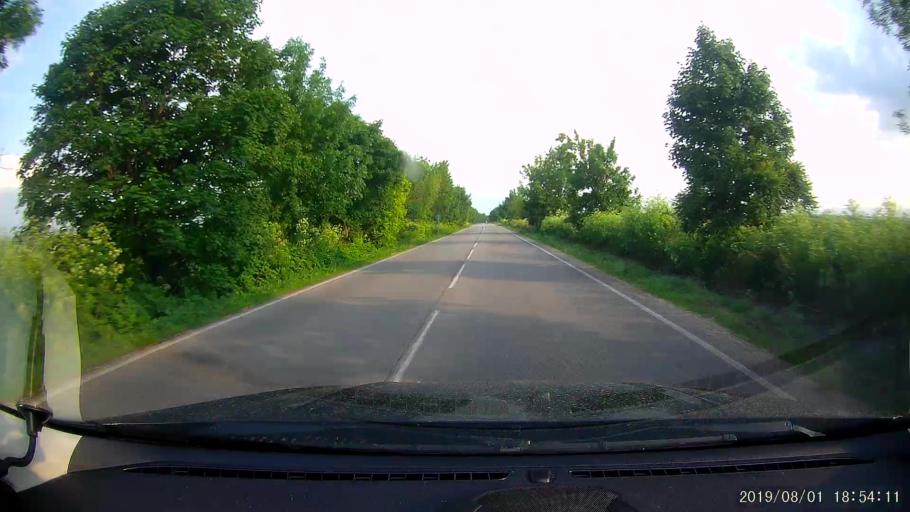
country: BG
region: Shumen
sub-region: Obshtina Shumen
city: Shumen
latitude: 43.2046
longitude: 27.0002
